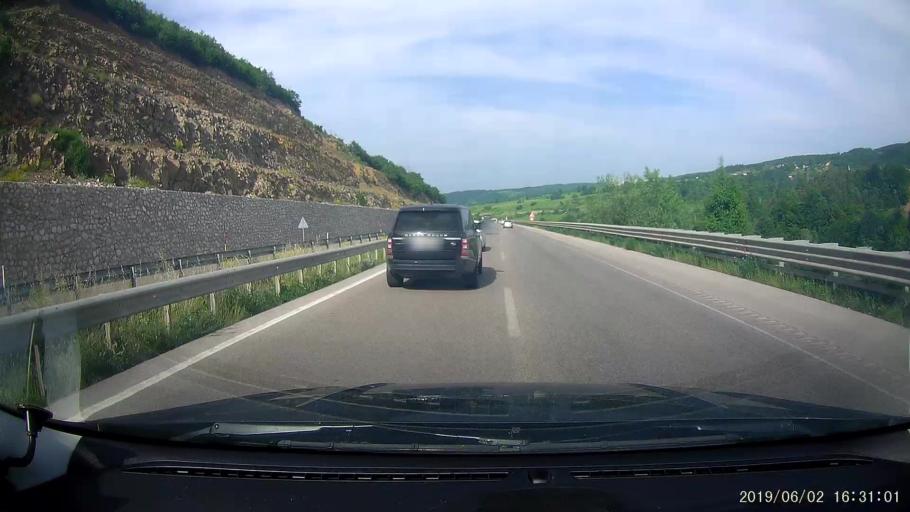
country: TR
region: Samsun
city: Ladik
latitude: 41.0296
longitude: 35.8938
